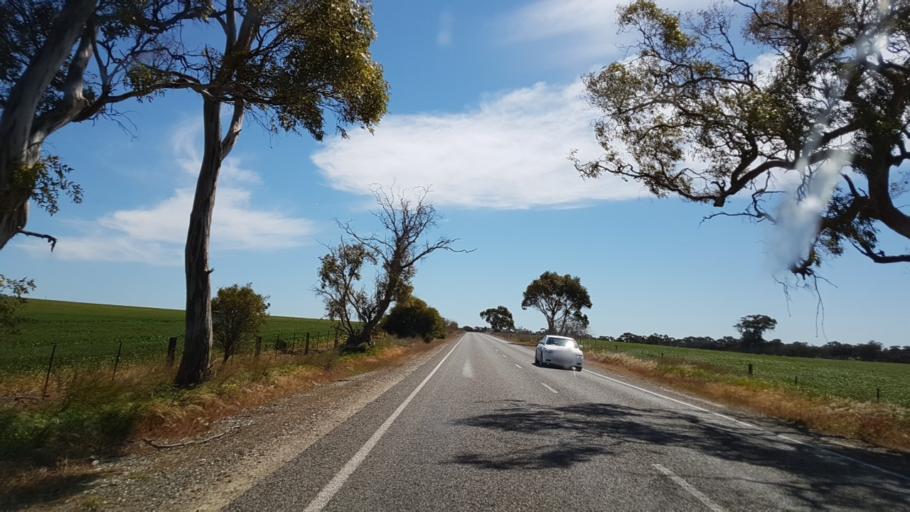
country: AU
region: South Australia
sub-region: Light
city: Kapunda
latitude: -34.2108
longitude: 138.7410
